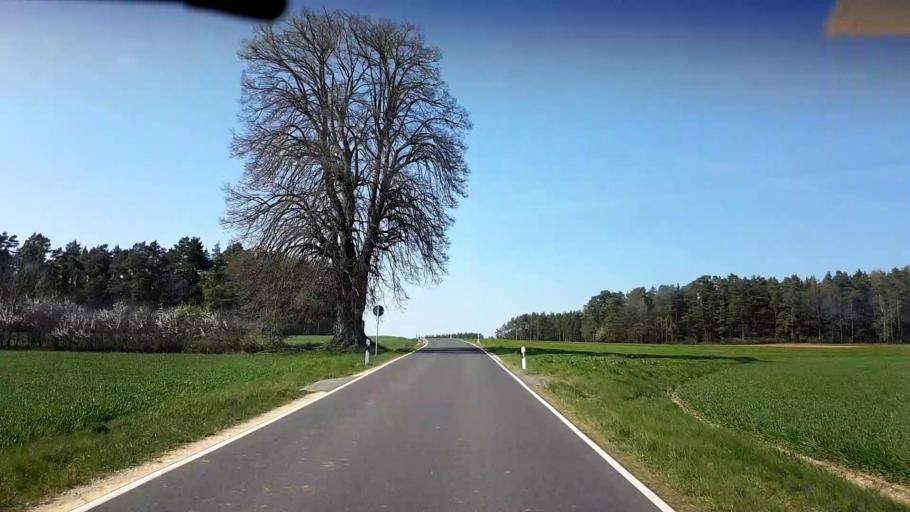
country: DE
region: Bavaria
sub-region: Upper Franconia
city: Pottenstein
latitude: 49.8016
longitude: 11.3740
